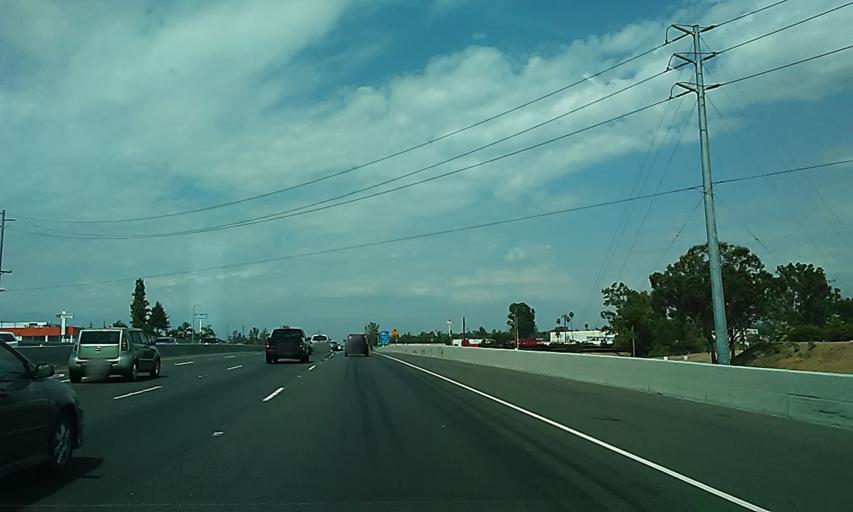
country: US
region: California
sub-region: Riverside County
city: Highgrove
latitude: 34.0298
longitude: -117.3293
